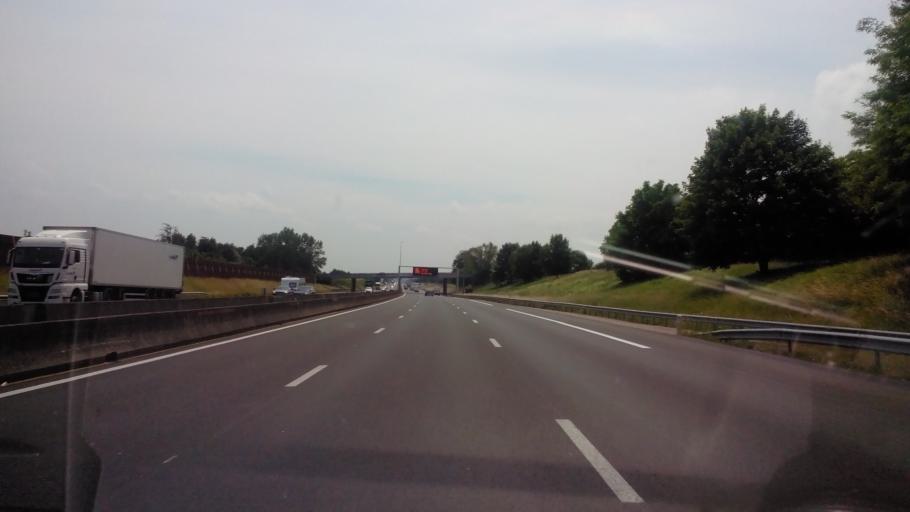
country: FR
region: Bourgogne
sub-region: Departement de Saone-et-Loire
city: Charnay-les-Macon
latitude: 46.3113
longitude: 4.7954
